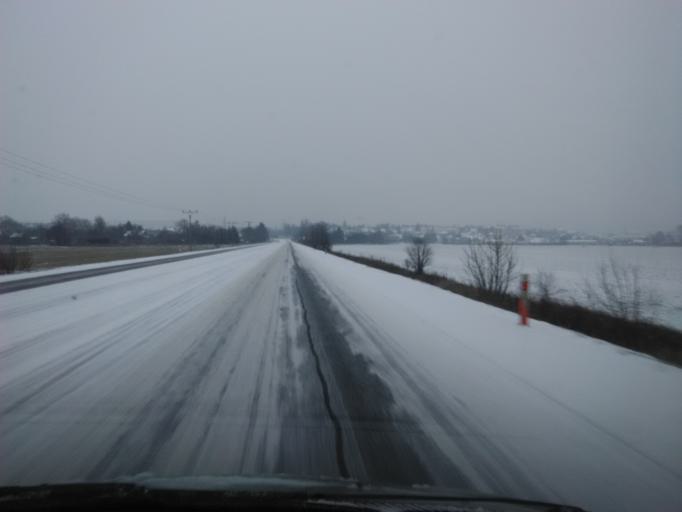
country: CZ
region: Olomoucky
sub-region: Okres Prerov
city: Hranice
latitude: 49.5498
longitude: 17.7070
